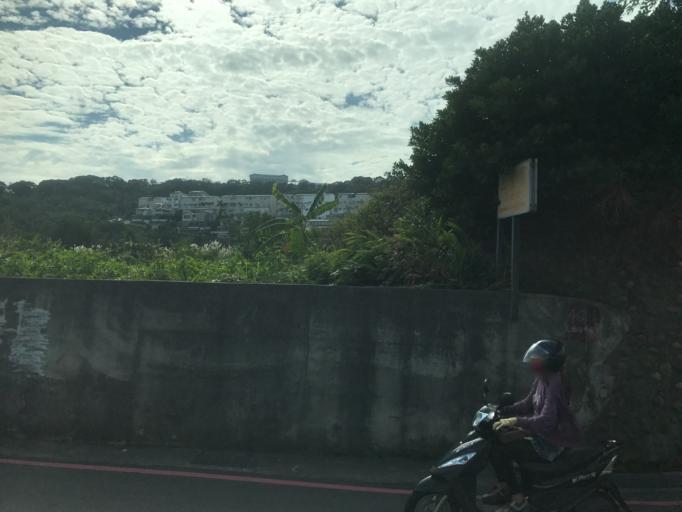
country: TW
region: Taiwan
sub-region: Hsinchu
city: Hsinchu
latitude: 24.7845
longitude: 120.9312
